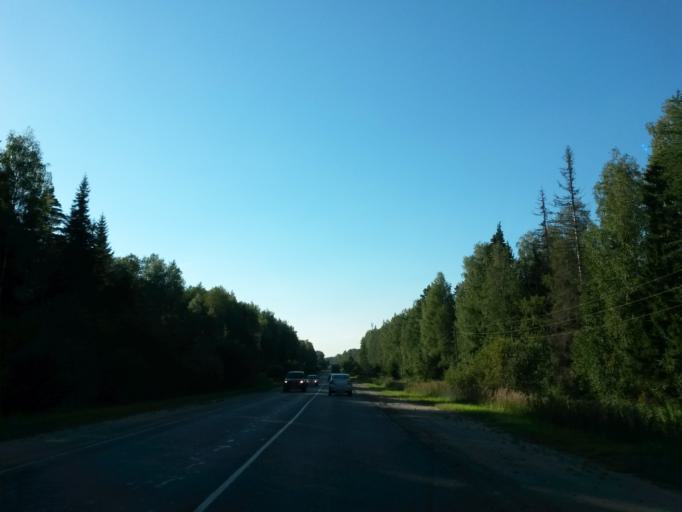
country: RU
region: Ivanovo
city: Novo-Talitsy
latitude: 57.0546
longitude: 40.7316
